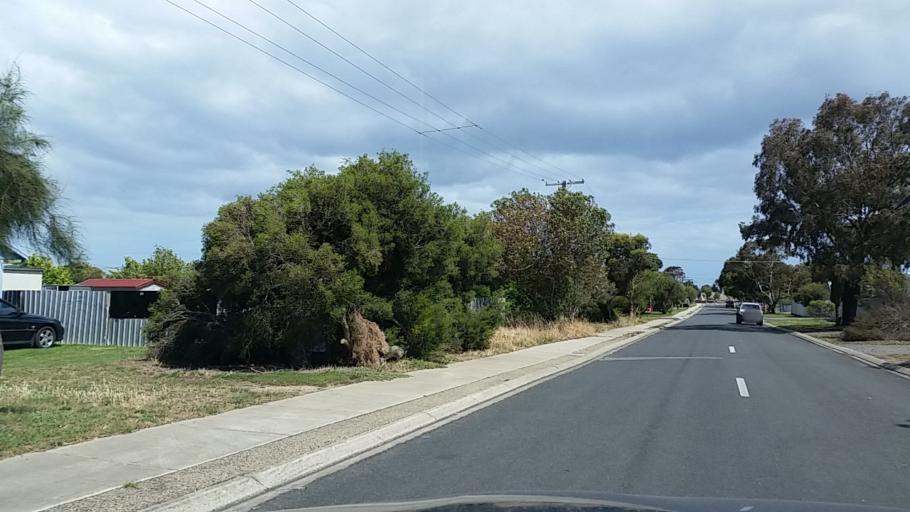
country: AU
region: South Australia
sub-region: Alexandrina
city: Port Elliot
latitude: -35.5202
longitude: 138.6779
